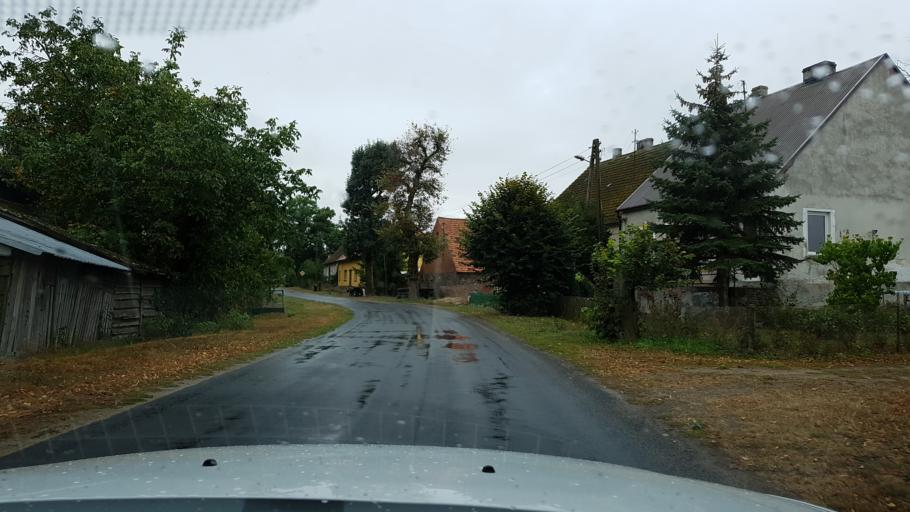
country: PL
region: West Pomeranian Voivodeship
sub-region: Powiat gryfinski
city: Cedynia
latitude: 52.8532
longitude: 14.2916
